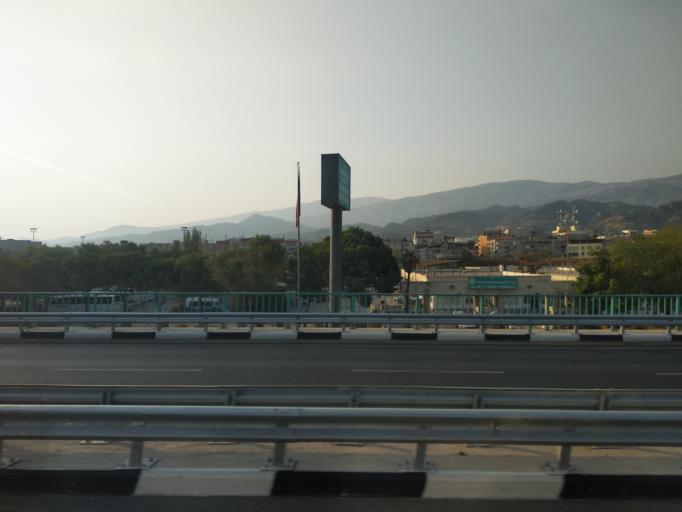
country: TR
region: Manisa
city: Salihli
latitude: 38.4887
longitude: 28.1349
